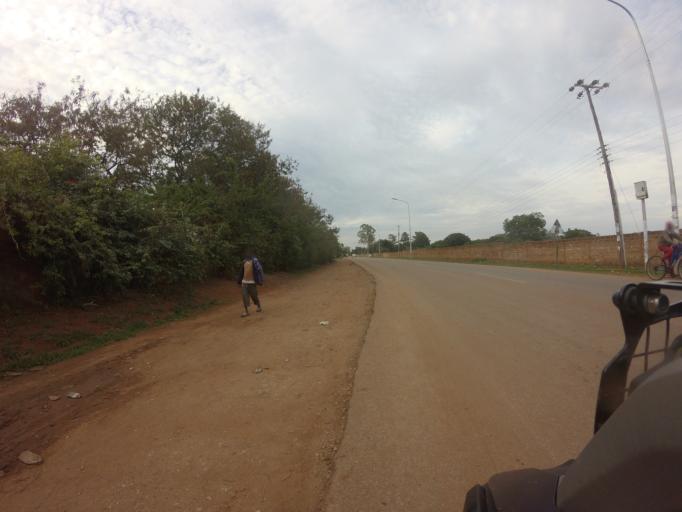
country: ZM
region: Lusaka
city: Lusaka
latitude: -15.5285
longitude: 28.2363
